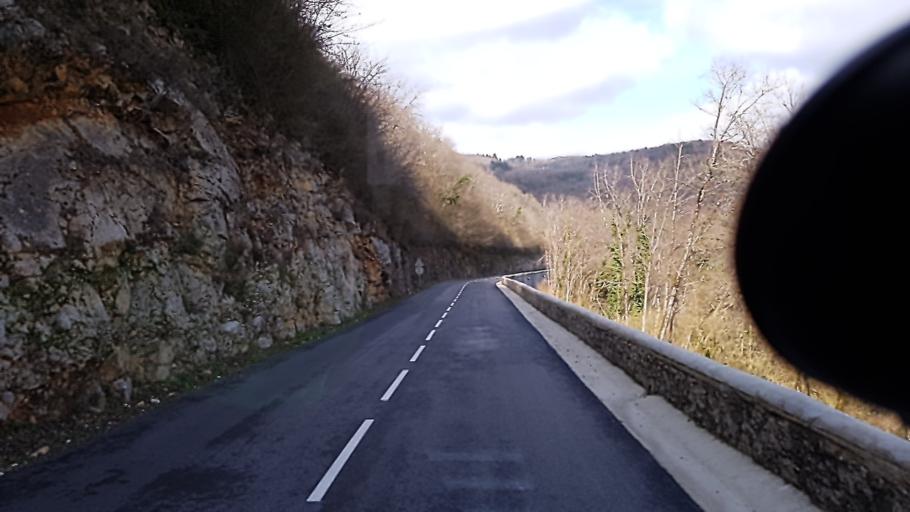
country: FR
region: Rhone-Alpes
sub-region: Departement de l'Ain
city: Izernore
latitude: 46.2402
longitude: 5.4887
